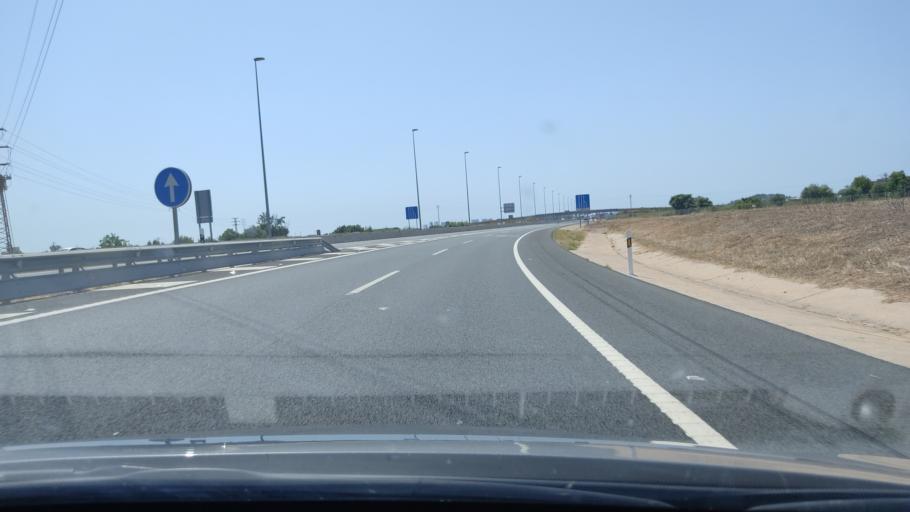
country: ES
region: Valencia
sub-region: Provincia de Valencia
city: Pucol
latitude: 39.6194
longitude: -0.2953
